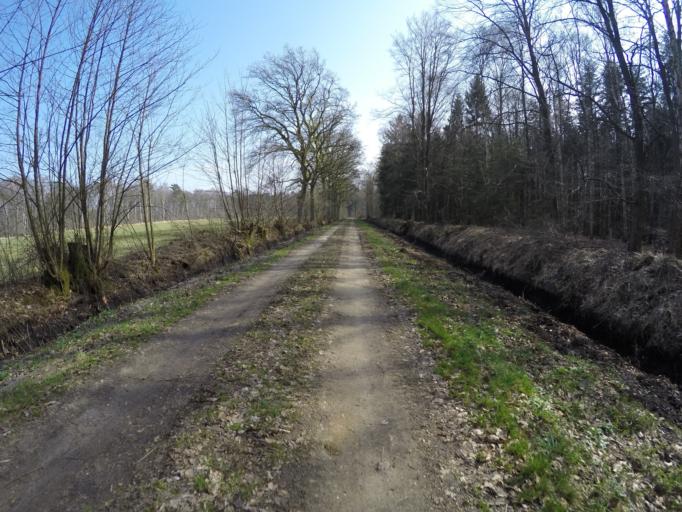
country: DE
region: Schleswig-Holstein
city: Borstel-Hohenraden
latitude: 53.7243
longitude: 9.8263
